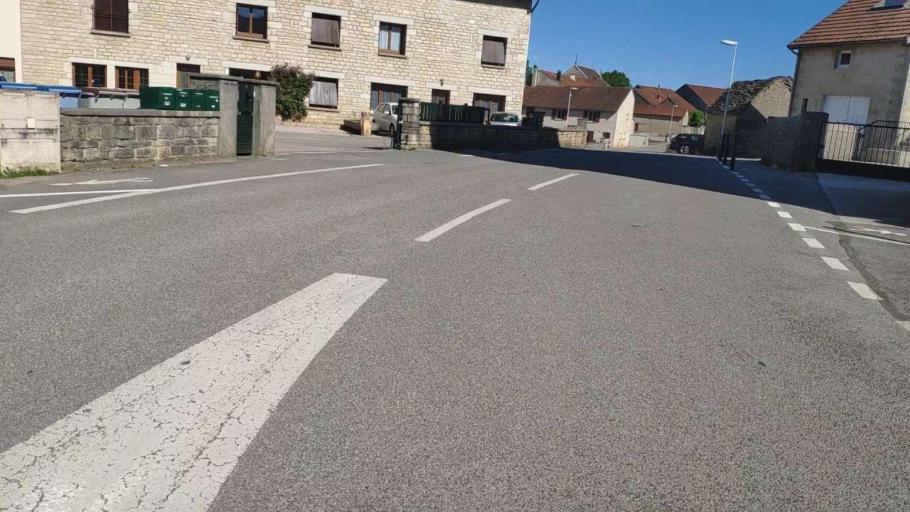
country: FR
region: Franche-Comte
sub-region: Departement du Jura
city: Perrigny
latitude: 46.6858
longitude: 5.6597
